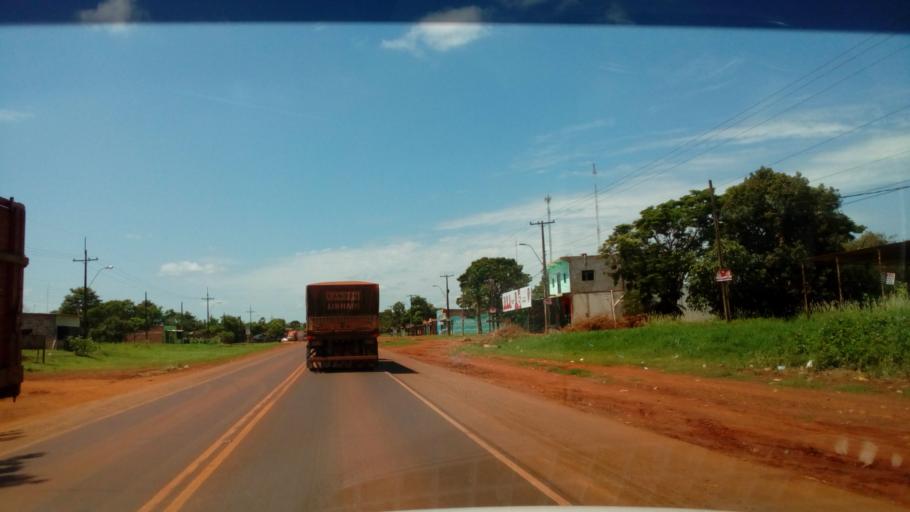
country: PY
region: Alto Parana
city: Colonia Yguazu
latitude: -25.4955
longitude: -54.8982
